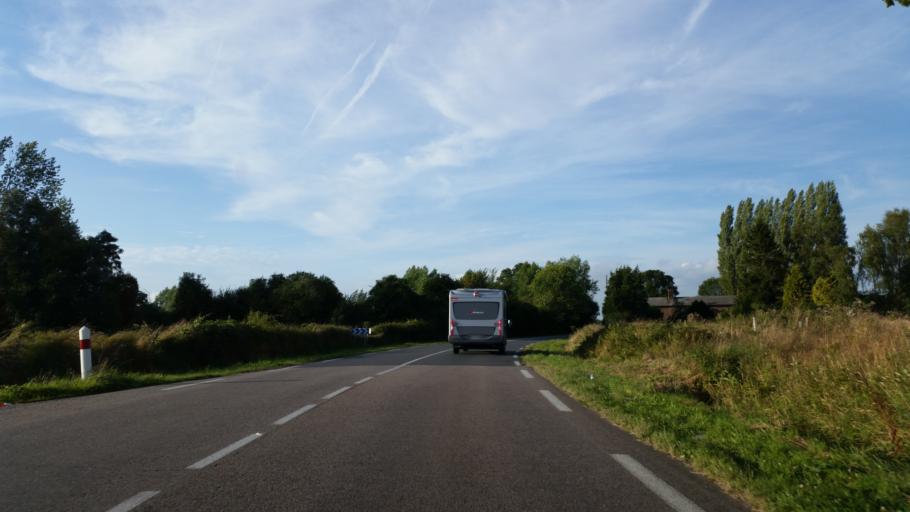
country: FR
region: Lower Normandy
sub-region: Departement du Calvados
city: Saint-Gatien-des-Bois
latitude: 49.3557
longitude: 0.1960
